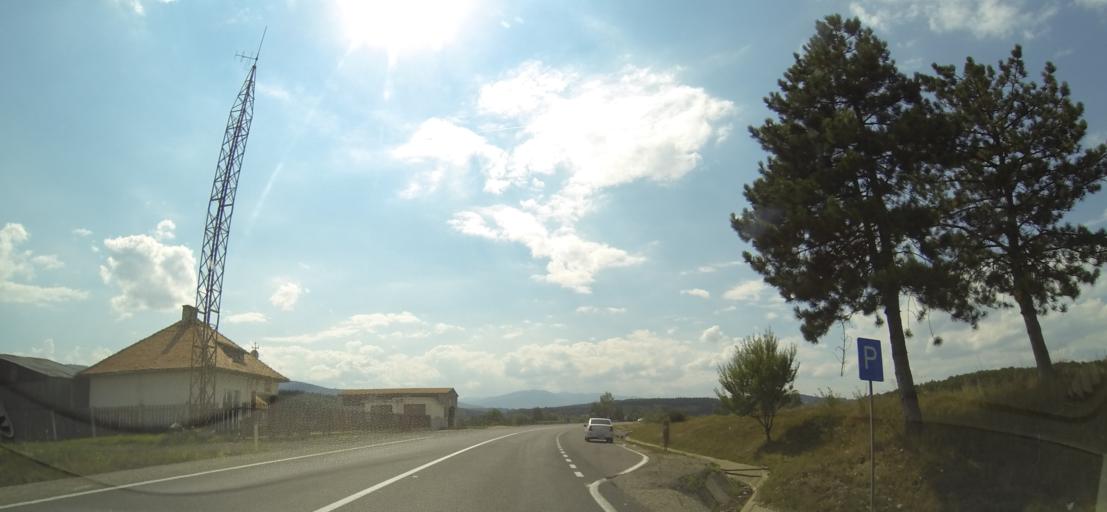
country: RO
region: Brasov
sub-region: Comuna Sinca Noua
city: Sinca Noua
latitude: 45.7468
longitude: 25.3055
